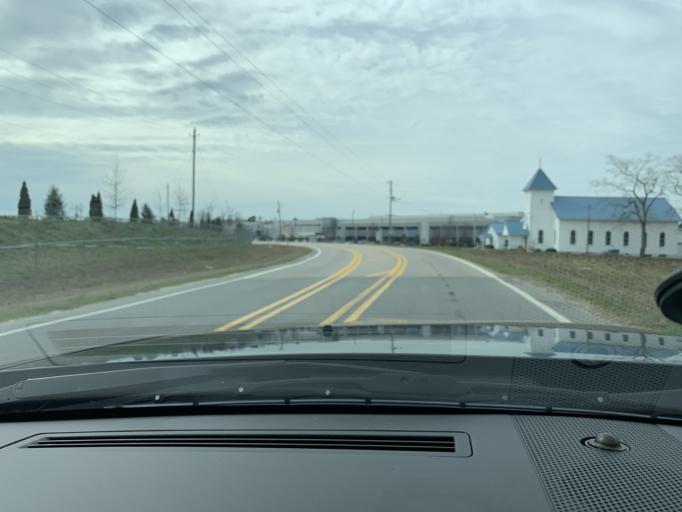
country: US
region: North Carolina
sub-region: Johnston County
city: Clayton
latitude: 35.6203
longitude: -78.4067
